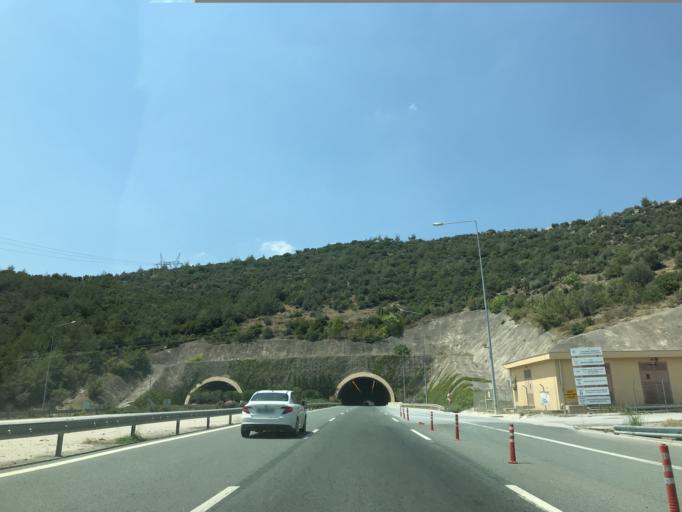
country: TR
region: Bursa
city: Gursu
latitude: 40.2537
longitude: 29.2196
